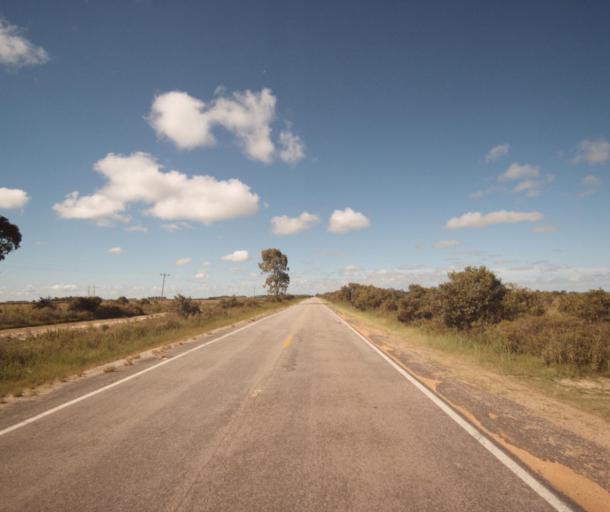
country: BR
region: Rio Grande do Sul
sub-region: Santa Vitoria Do Palmar
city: Santa Vitoria do Palmar
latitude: -33.3817
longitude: -53.1988
